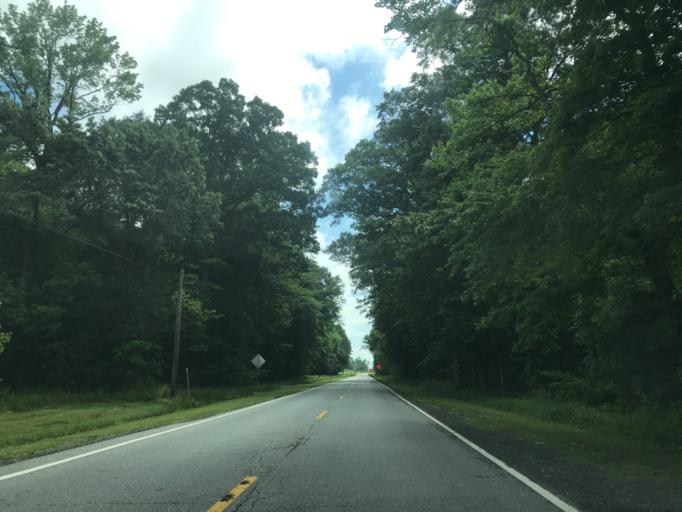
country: US
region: Maryland
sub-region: Caroline County
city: Ridgely
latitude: 38.9173
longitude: -75.9239
